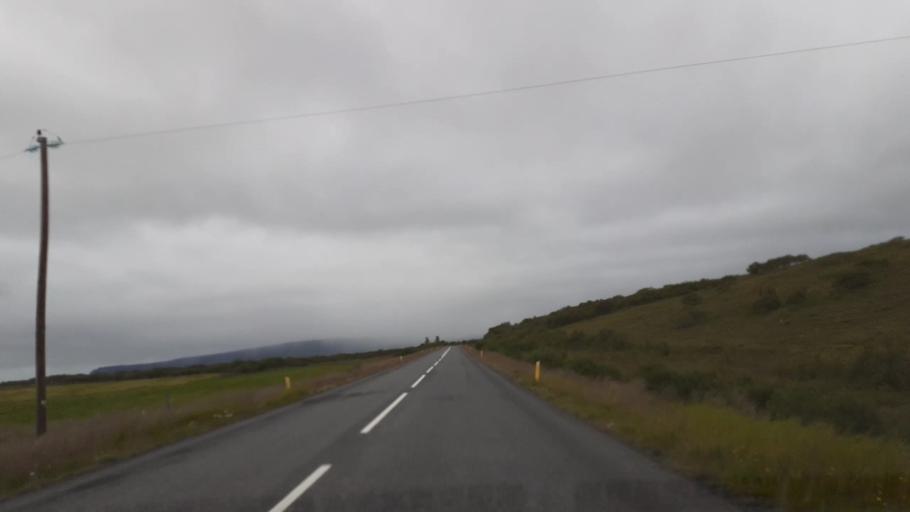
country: IS
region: Northeast
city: Husavik
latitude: 66.0678
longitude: -16.4406
